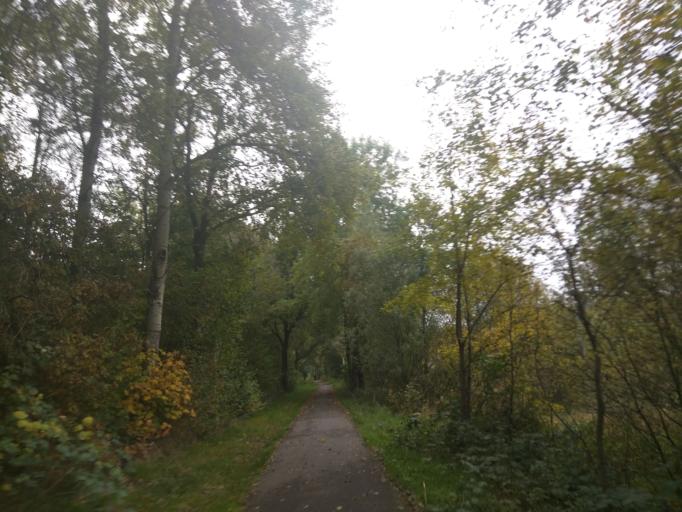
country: DK
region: Central Jutland
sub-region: Silkeborg Kommune
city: Silkeborg
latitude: 56.2351
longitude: 9.5246
